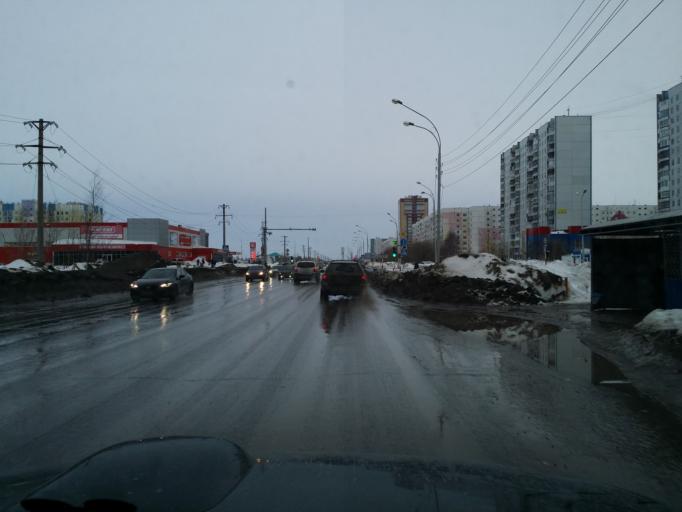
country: RU
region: Khanty-Mansiyskiy Avtonomnyy Okrug
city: Nizhnevartovsk
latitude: 60.9310
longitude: 76.6087
